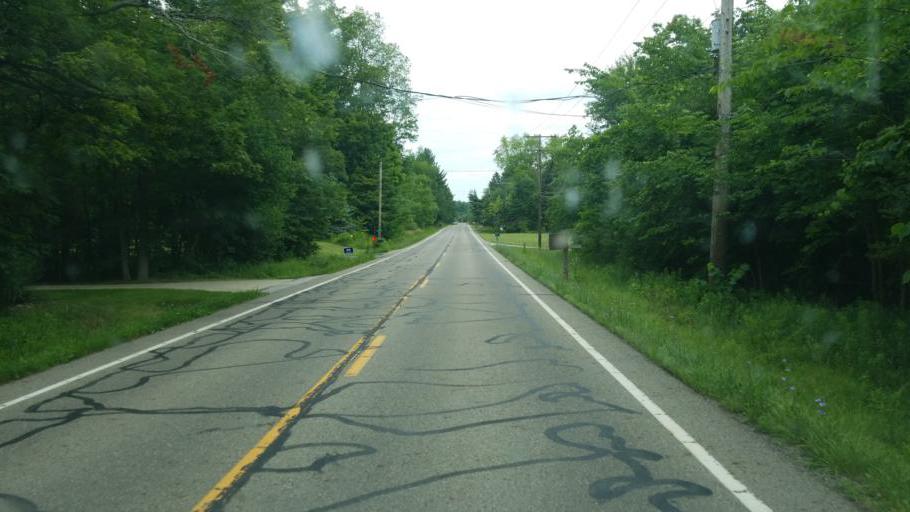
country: US
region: Ohio
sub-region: Geauga County
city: Burton
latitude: 41.4415
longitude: -81.2464
